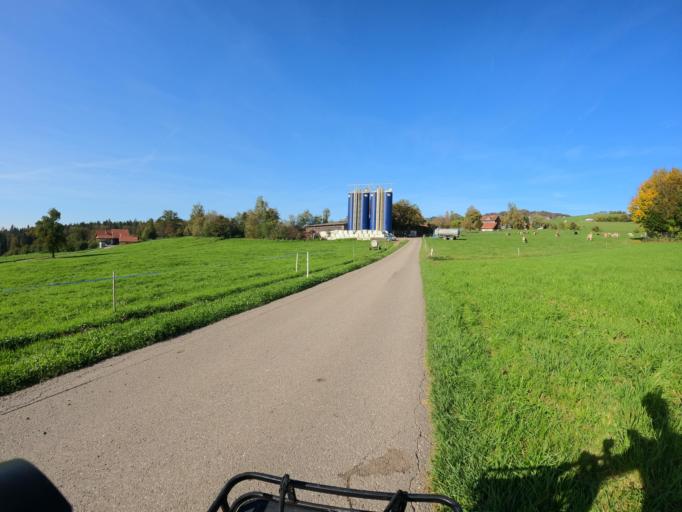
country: CH
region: Zug
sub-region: Zug
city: Baar
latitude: 47.2145
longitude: 8.5561
